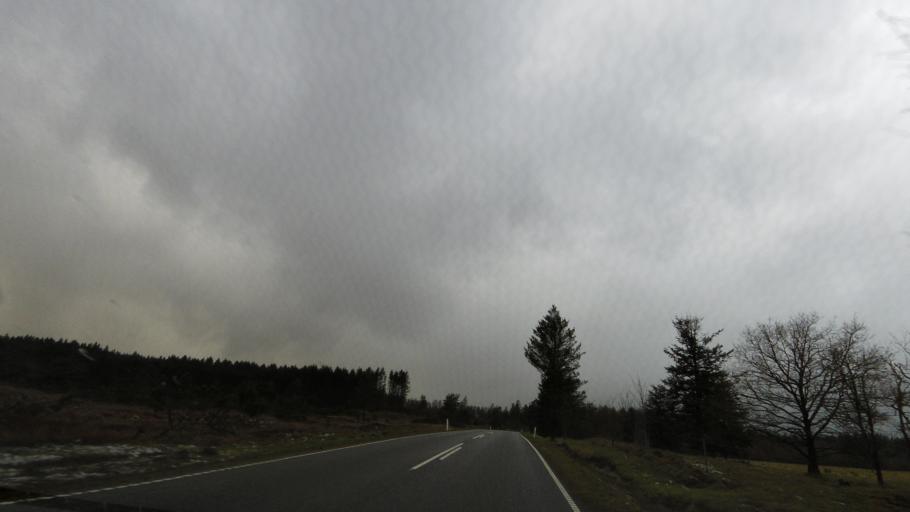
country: DK
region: Central Jutland
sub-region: Ikast-Brande Kommune
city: Brande
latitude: 56.0007
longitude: 9.1837
